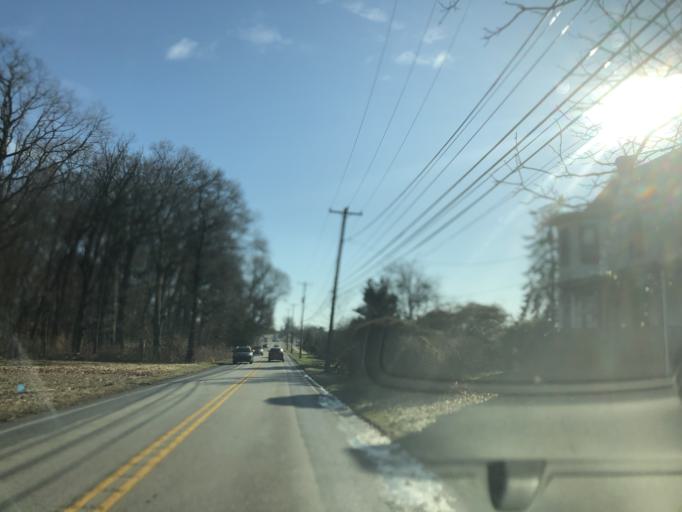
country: US
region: Pennsylvania
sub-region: Chester County
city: Toughkenamon
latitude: 39.8138
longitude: -75.7520
